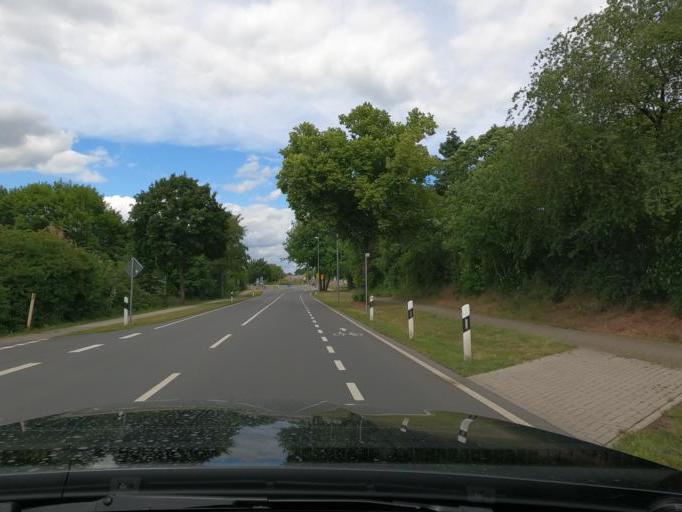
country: DE
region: Lower Saxony
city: Burgdorf
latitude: 52.4575
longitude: 9.9939
